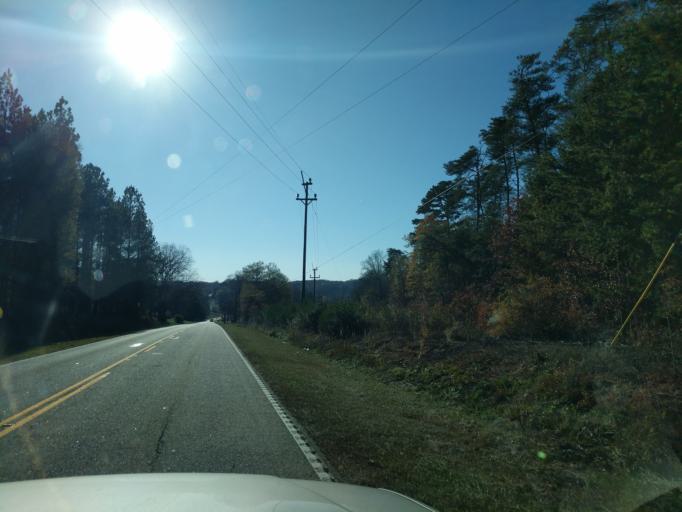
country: US
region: South Carolina
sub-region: Spartanburg County
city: Landrum
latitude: 35.1250
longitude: -82.1382
